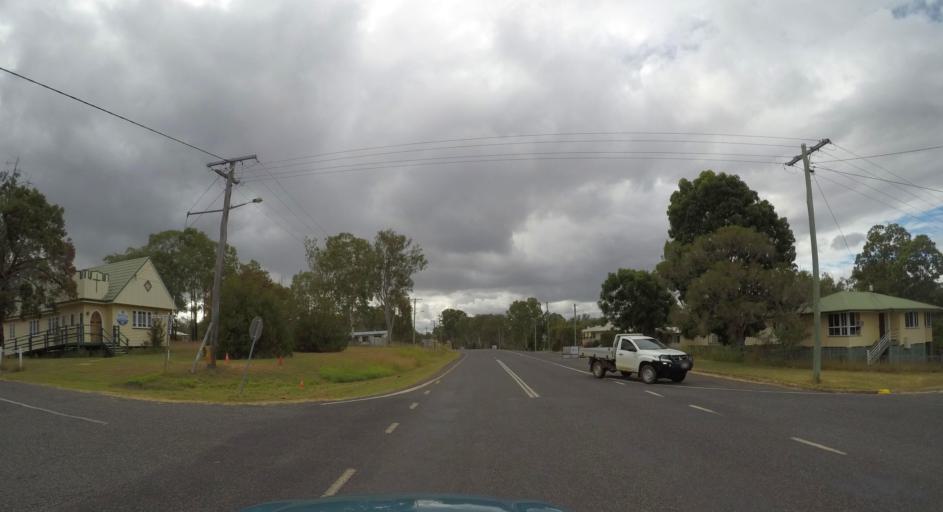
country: AU
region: Queensland
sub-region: North Burnett
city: Gayndah
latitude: -25.3662
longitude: 151.1210
